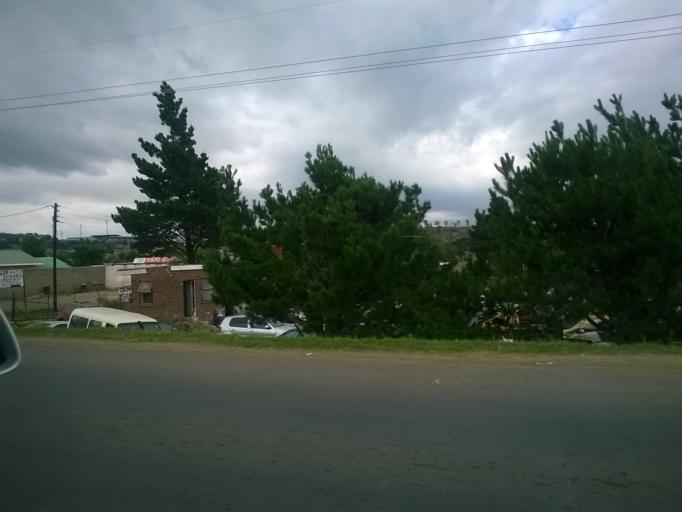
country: LS
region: Maseru
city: Maseru
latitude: -29.3041
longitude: 27.5159
